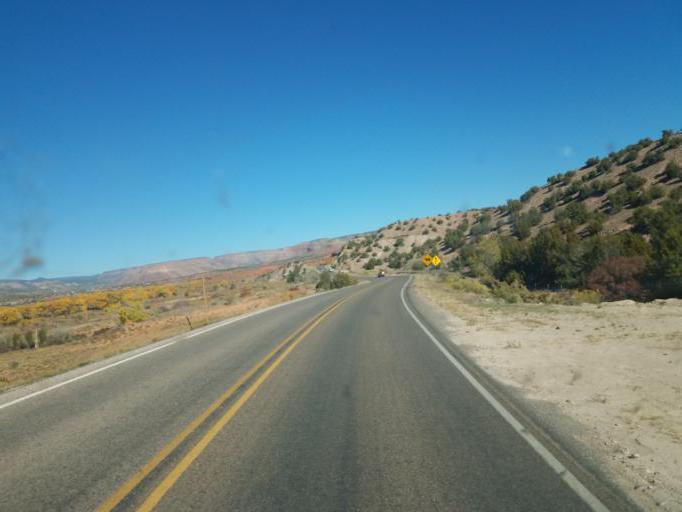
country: US
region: New Mexico
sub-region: Sandoval County
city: Jemez Pueblo
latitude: 35.6286
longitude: -106.7245
